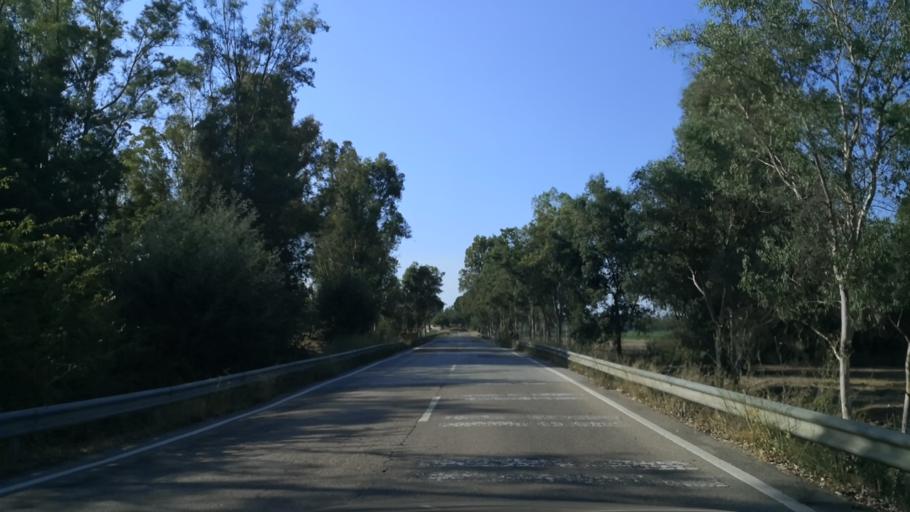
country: PT
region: Santarem
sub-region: Coruche
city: Coruche
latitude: 38.9909
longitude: -8.5534
